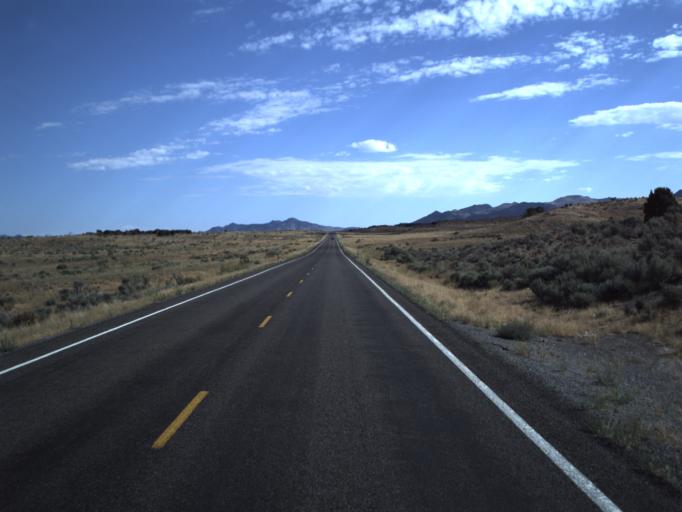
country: US
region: Utah
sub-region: Juab County
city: Mona
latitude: 39.7414
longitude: -112.1883
